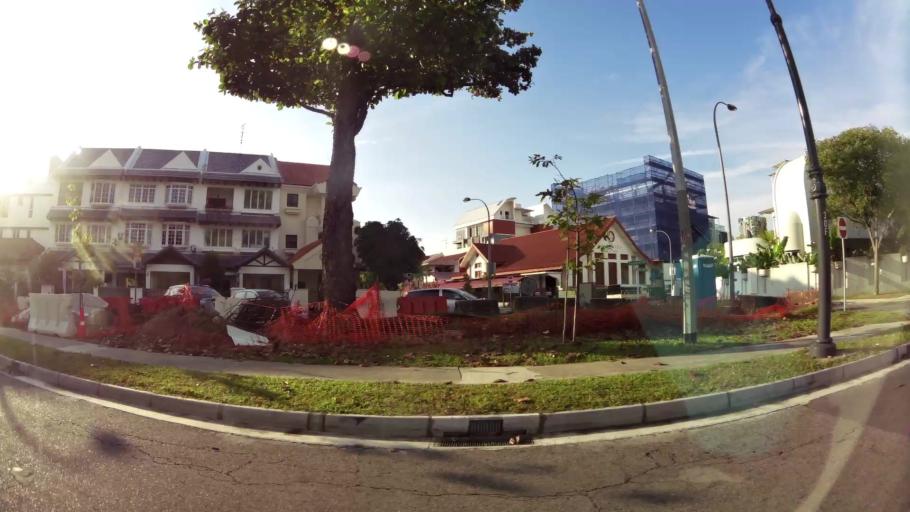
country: SG
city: Singapore
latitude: 1.3095
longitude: 103.9009
